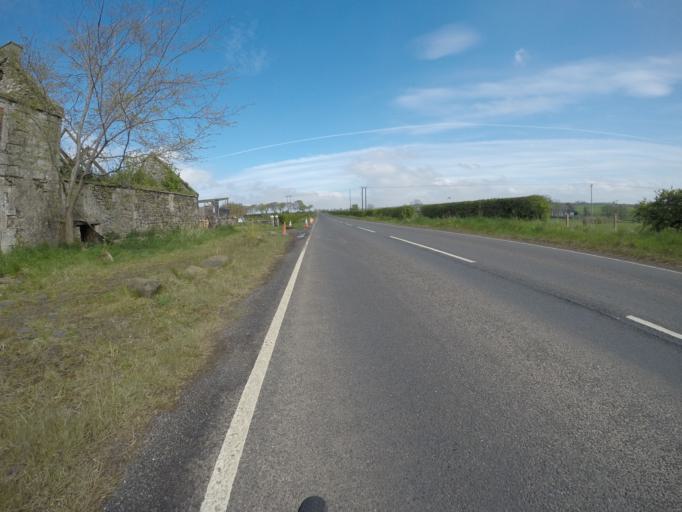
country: GB
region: Scotland
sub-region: East Ayrshire
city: Kilmaurs
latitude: 55.6624
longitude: -4.5467
